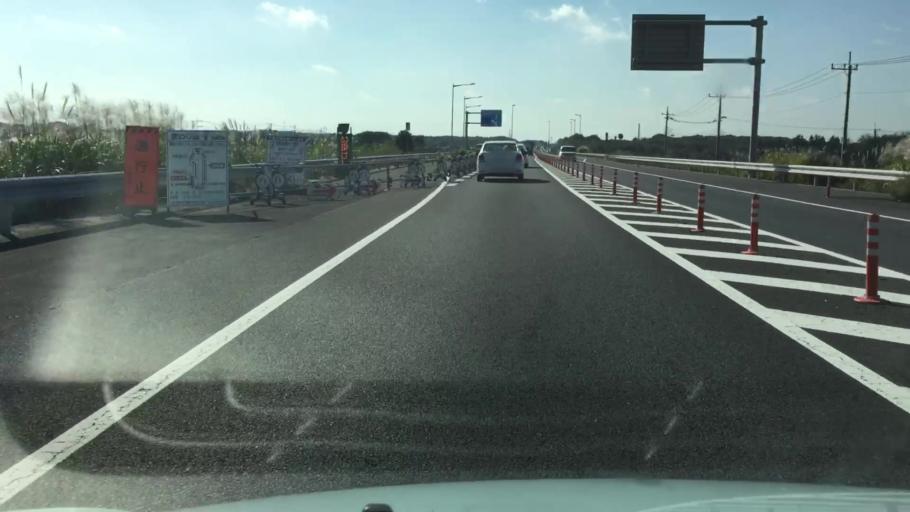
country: JP
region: Tochigi
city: Mooka
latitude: 36.5162
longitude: 139.9861
